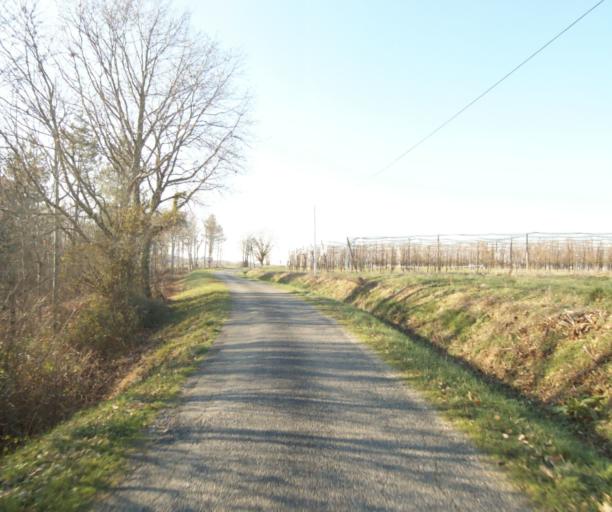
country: FR
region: Midi-Pyrenees
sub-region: Departement du Tarn-et-Garonne
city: Moissac
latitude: 44.1455
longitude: 1.0638
